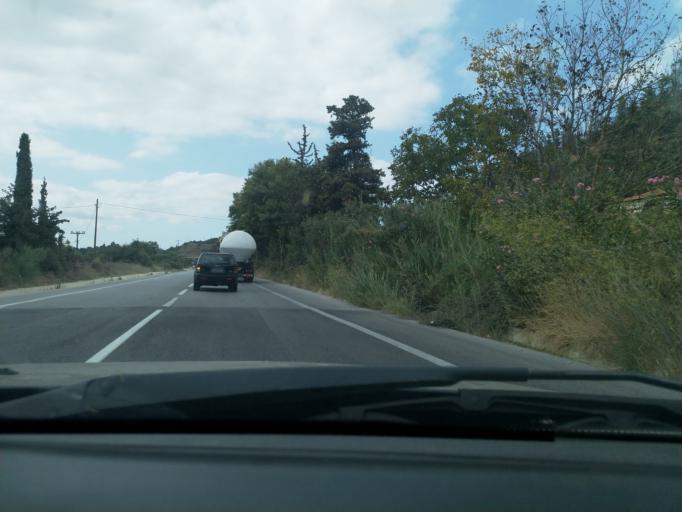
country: GR
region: Crete
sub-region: Nomos Chanias
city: Georgioupolis
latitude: 35.3744
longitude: 24.2099
